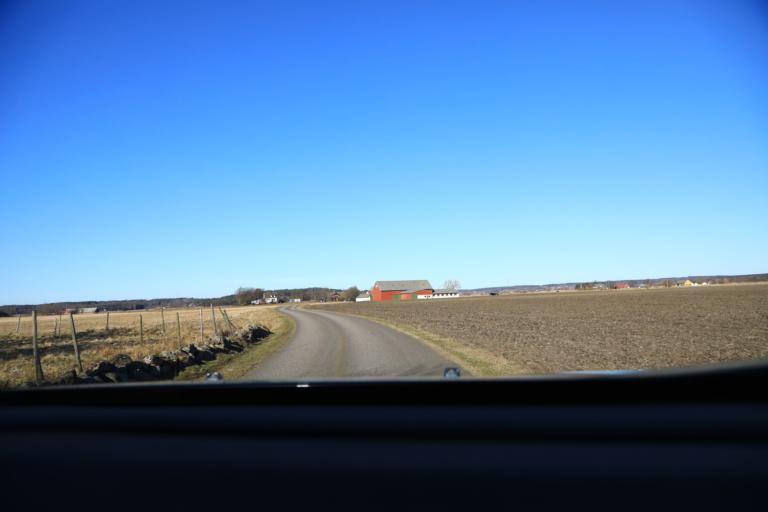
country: SE
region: Halland
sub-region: Kungsbacka Kommun
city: Frillesas
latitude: 57.2318
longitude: 12.1474
